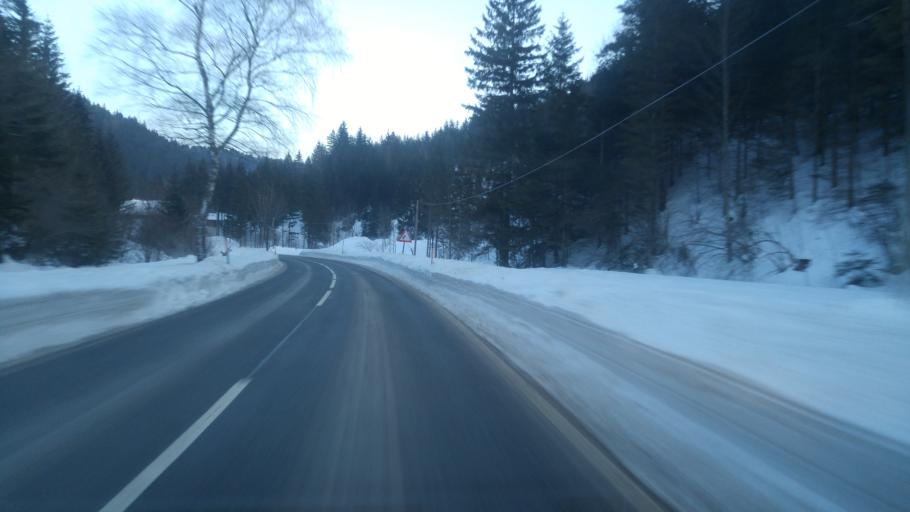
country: AT
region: Lower Austria
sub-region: Politischer Bezirk Wiener Neustadt
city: Rohr im Gebirge
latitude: 47.8776
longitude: 15.7683
